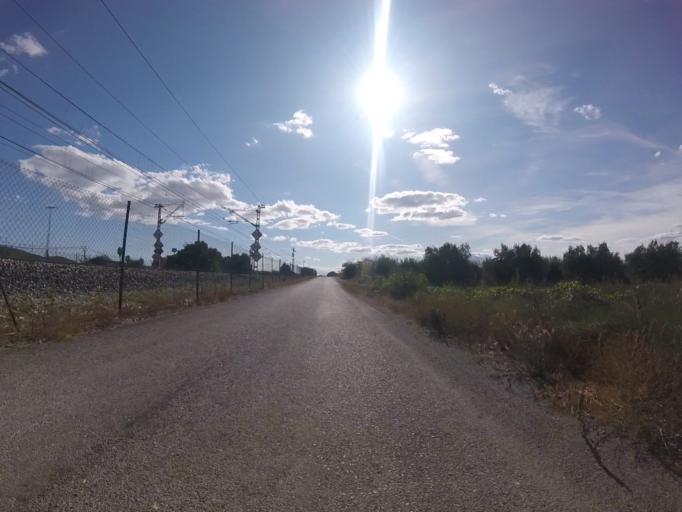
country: ES
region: Valencia
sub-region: Provincia de Castello
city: Alcala de Xivert
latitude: 40.2967
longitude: 0.2256
